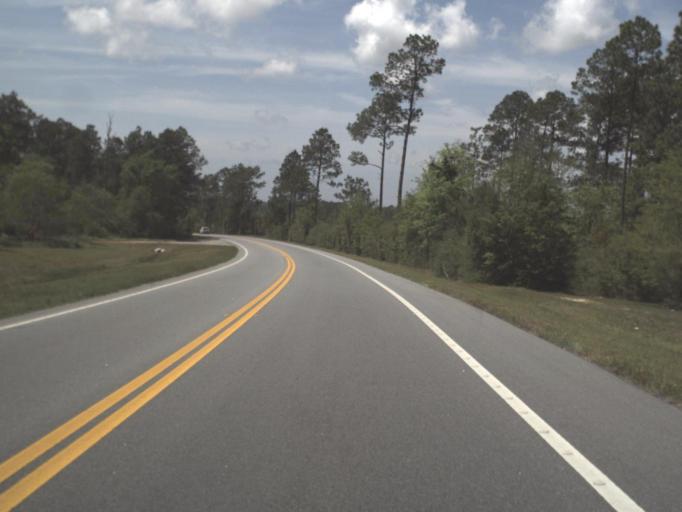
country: US
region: Florida
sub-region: Escambia County
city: Cantonment
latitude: 30.5339
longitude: -87.4219
